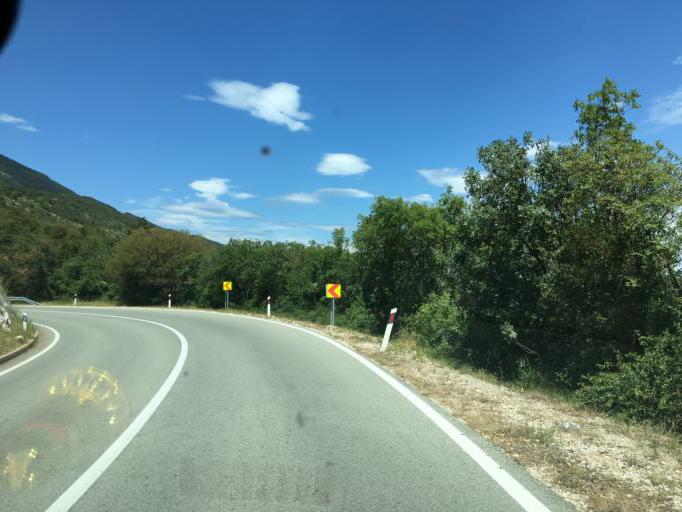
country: HR
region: Istarska
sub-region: Grad Labin
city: Rabac
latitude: 45.1481
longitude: 14.2134
